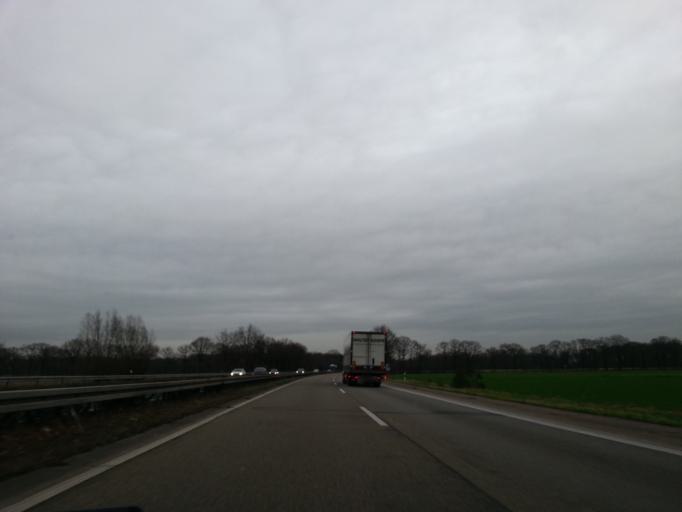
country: DE
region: North Rhine-Westphalia
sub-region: Regierungsbezirk Dusseldorf
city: Wesel
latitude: 51.6817
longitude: 6.7014
